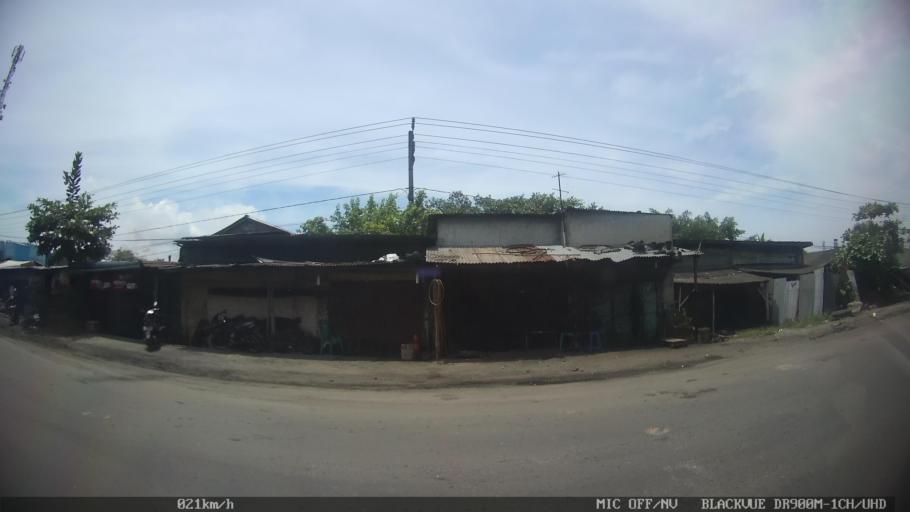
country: ID
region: North Sumatra
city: Belawan
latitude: 3.7810
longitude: 98.6914
